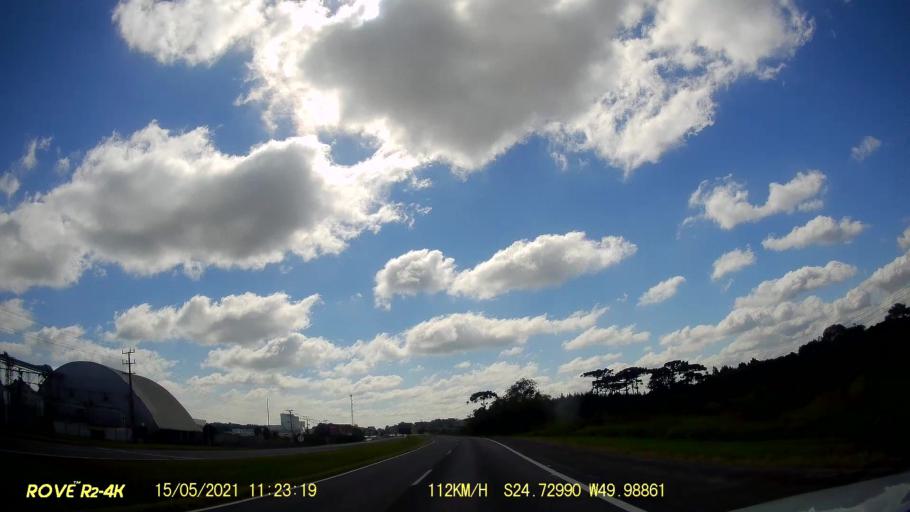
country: BR
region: Parana
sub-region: Castro
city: Castro
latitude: -24.7302
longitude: -49.9887
